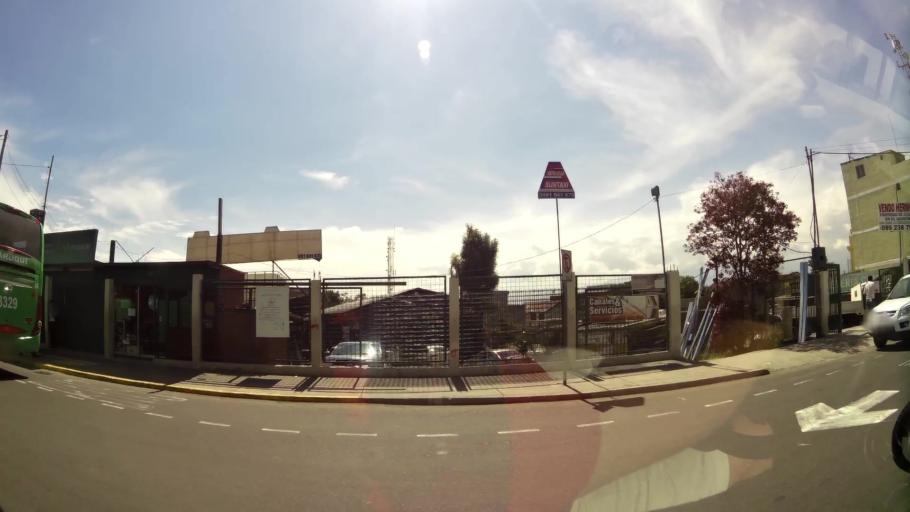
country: EC
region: Pichincha
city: Quito
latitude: -0.2006
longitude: -78.4333
